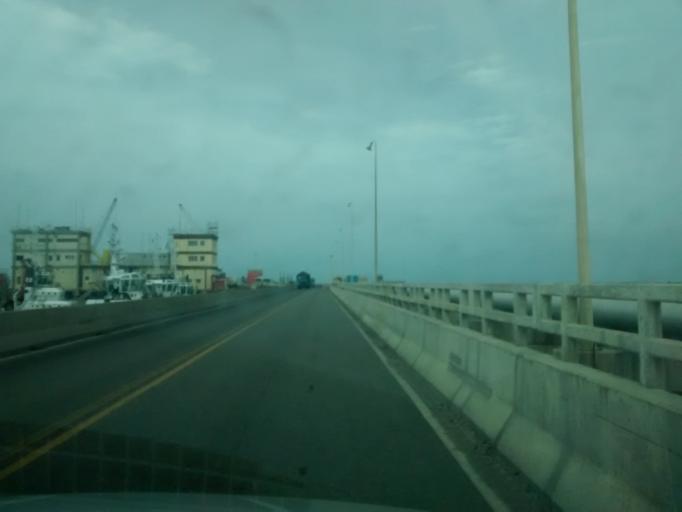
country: BR
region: Ceara
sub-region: Caucaia
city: Cambebba
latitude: -3.5343
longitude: -38.7970
